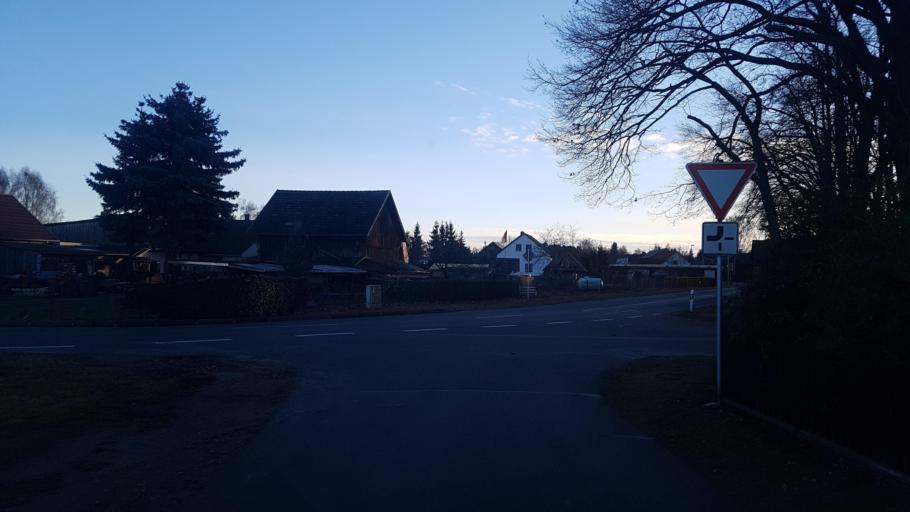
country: DE
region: Brandenburg
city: Drachhausen
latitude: 51.8908
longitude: 14.3123
